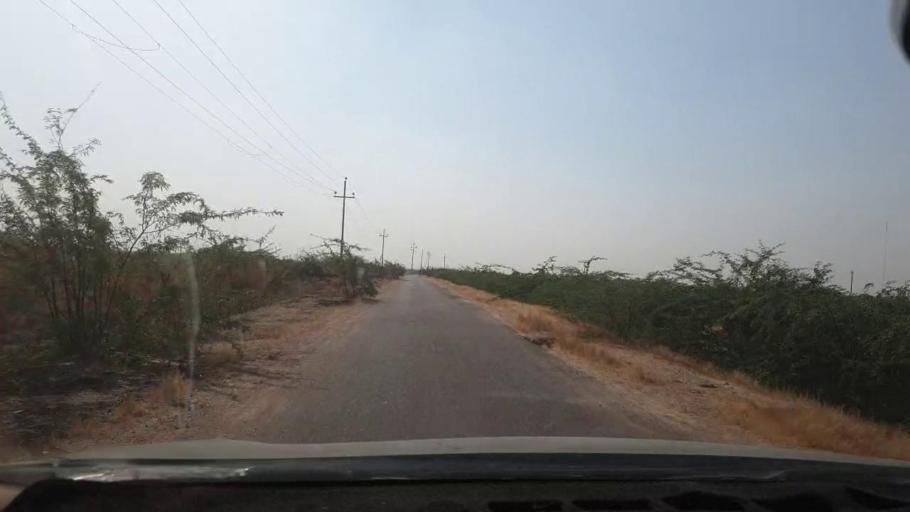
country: PK
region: Sindh
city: Malir Cantonment
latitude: 25.1095
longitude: 67.2036
